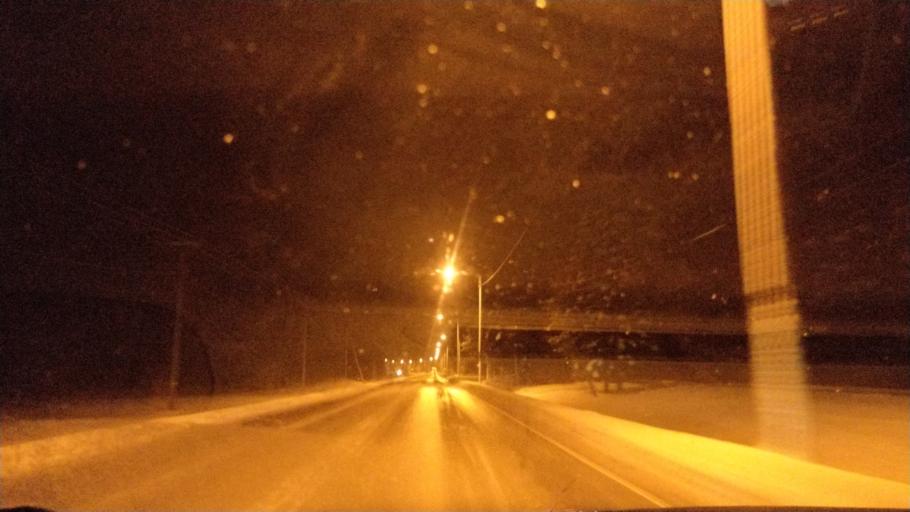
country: FI
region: Lapland
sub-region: Rovaniemi
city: Rovaniemi
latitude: 66.3061
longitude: 25.3579
